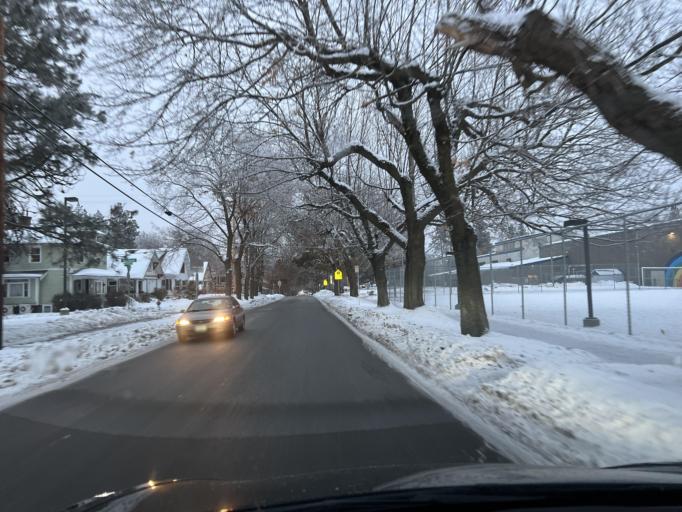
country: US
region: Washington
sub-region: Spokane County
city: Spokane
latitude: 47.6427
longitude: -117.4160
